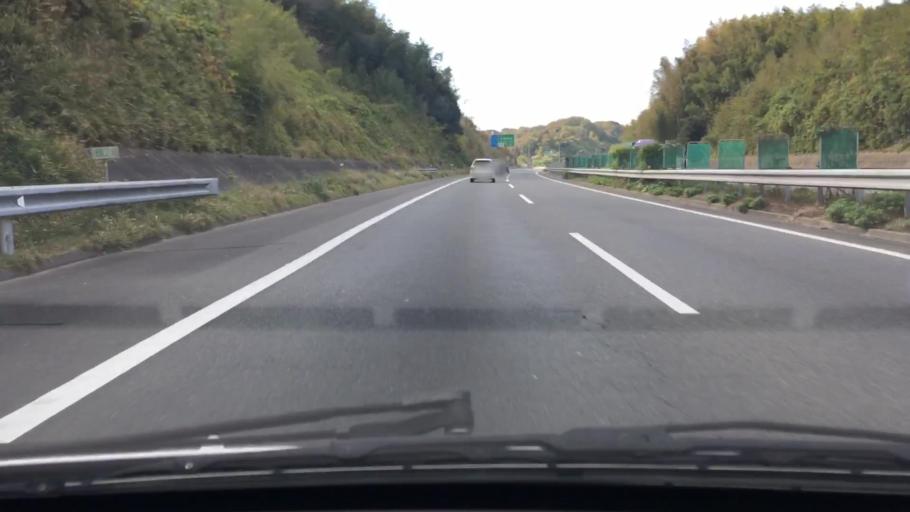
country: JP
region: Chiba
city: Kisarazu
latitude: 35.3894
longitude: 140.0016
